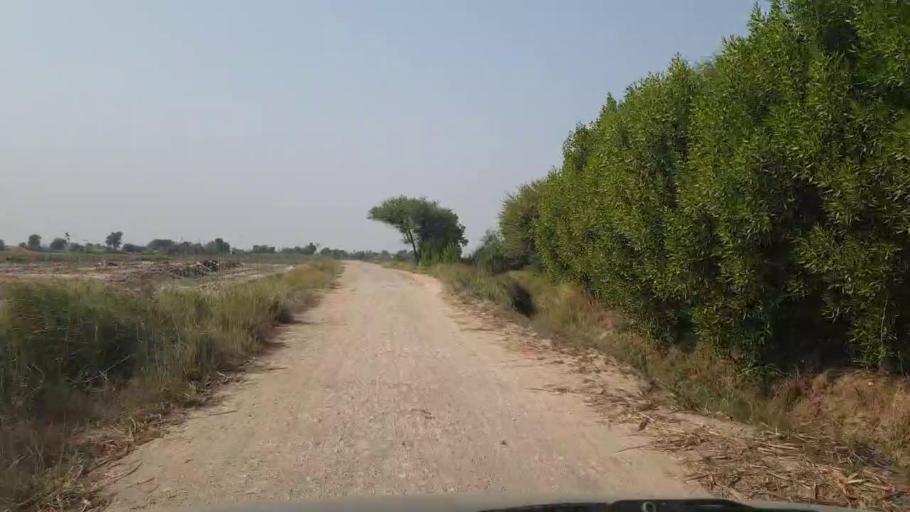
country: PK
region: Sindh
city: Tando Muhammad Khan
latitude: 25.0501
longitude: 68.3704
